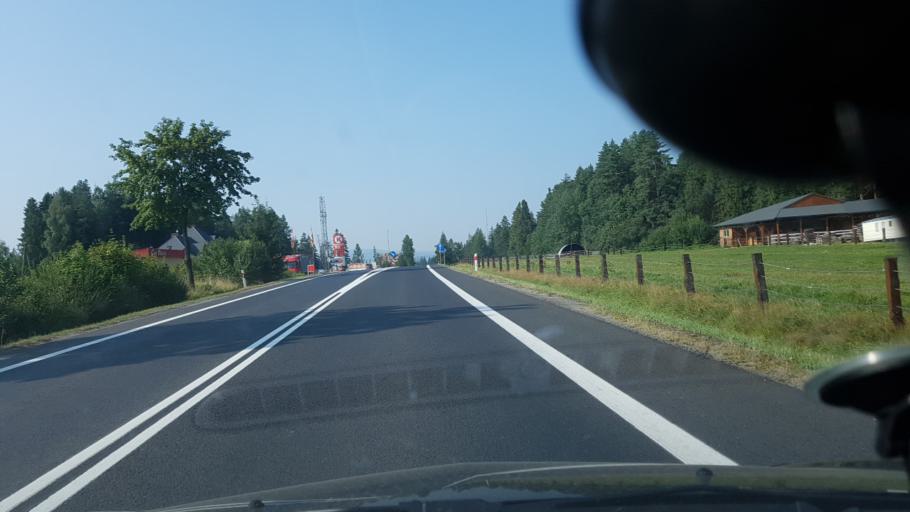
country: PL
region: Lesser Poland Voivodeship
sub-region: Powiat nowotarski
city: Chyzne
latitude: 49.4141
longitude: 19.6645
